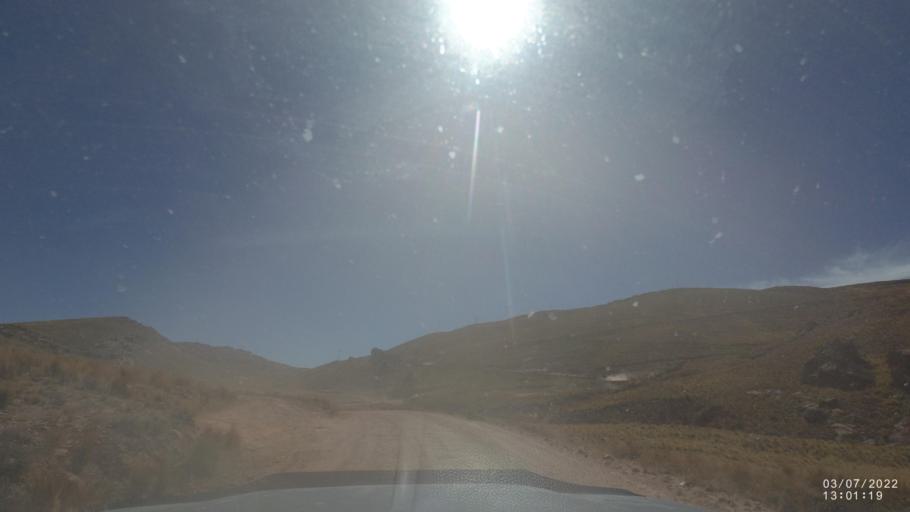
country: BO
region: Cochabamba
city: Colchani
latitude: -17.7095
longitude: -66.6908
